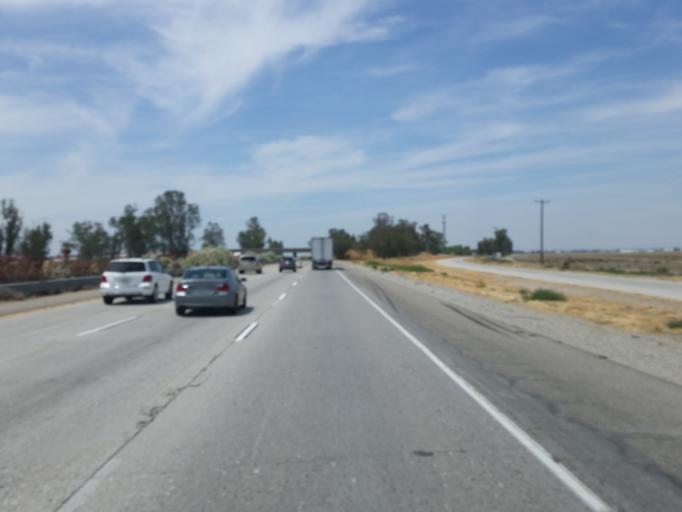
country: US
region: California
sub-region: Kern County
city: Greenfield
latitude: 35.1691
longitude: -119.0030
